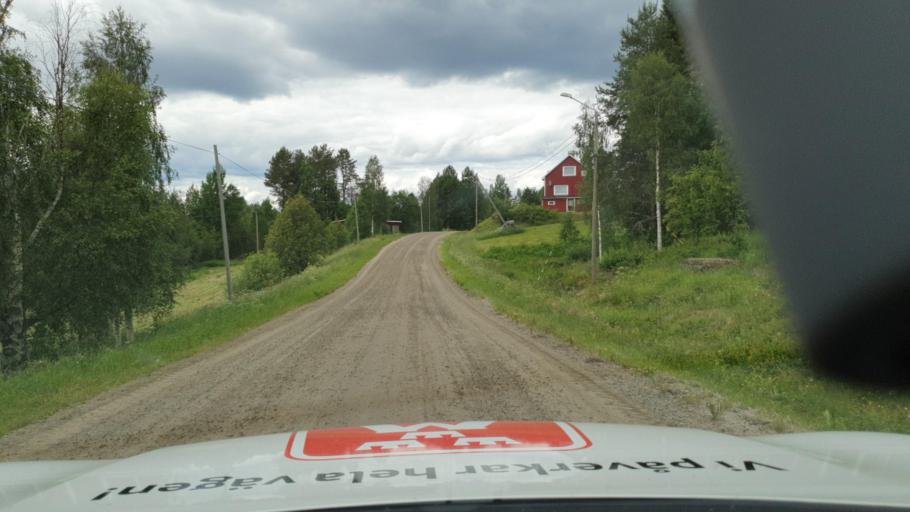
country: SE
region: Vaesterbotten
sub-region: Bjurholms Kommun
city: Bjurholm
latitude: 63.8151
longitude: 19.0321
